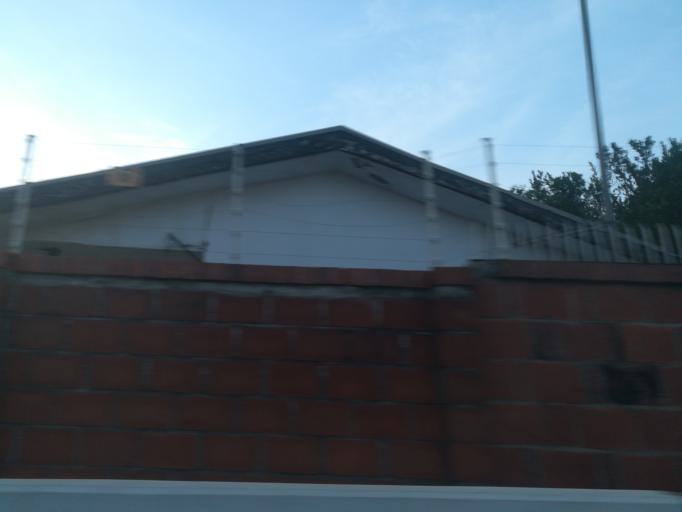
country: NG
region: Abuja Federal Capital Territory
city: Abuja
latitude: 9.0787
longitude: 7.3947
